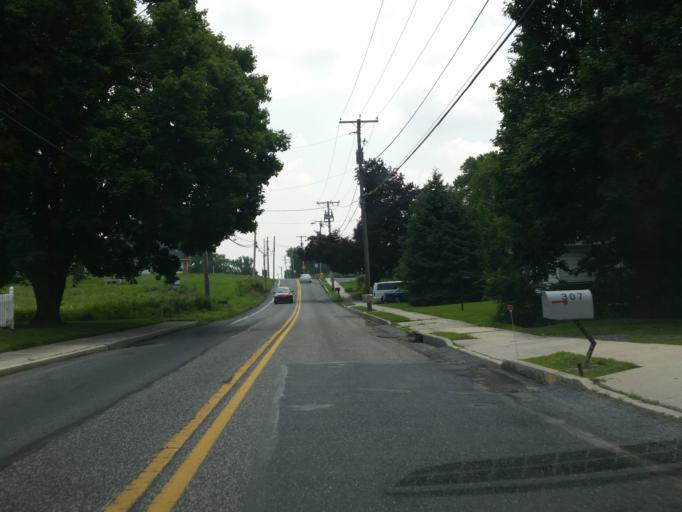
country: US
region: Pennsylvania
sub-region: Dauphin County
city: Palmdale
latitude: 40.2980
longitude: -76.6069
